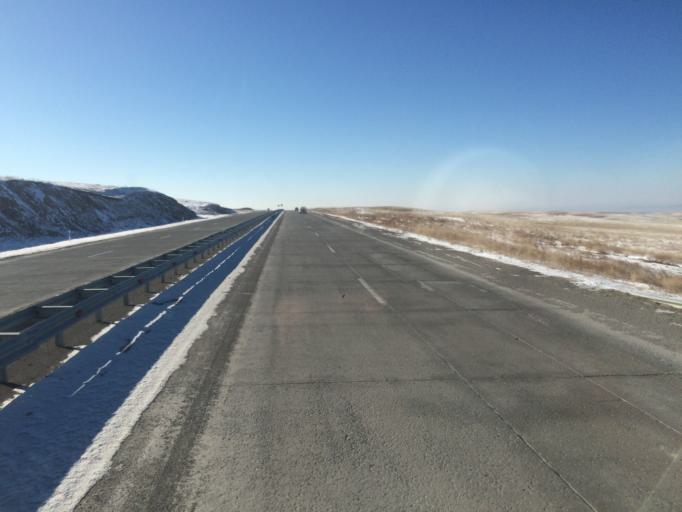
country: KZ
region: Zhambyl
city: Georgiyevka
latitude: 43.3750
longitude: 74.7508
